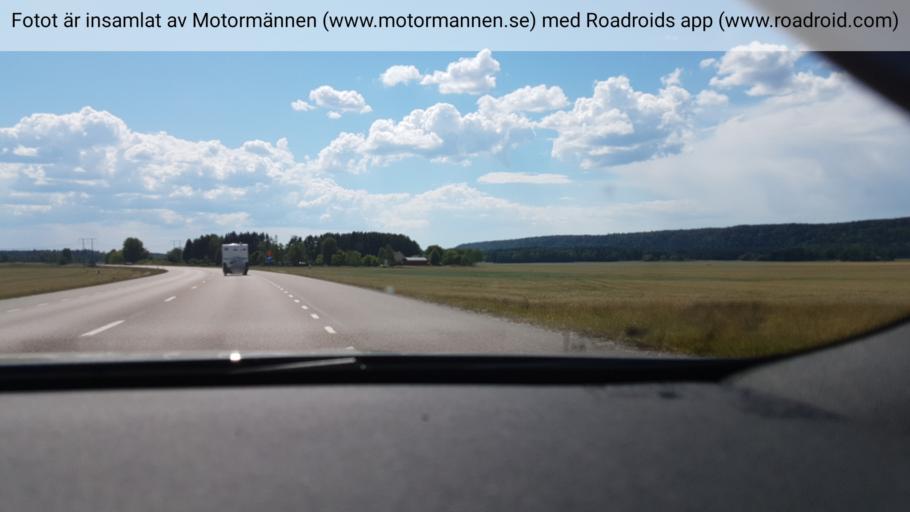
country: SE
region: Vaestra Goetaland
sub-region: Grastorps Kommun
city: Graestorp
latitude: 58.3202
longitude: 12.5691
